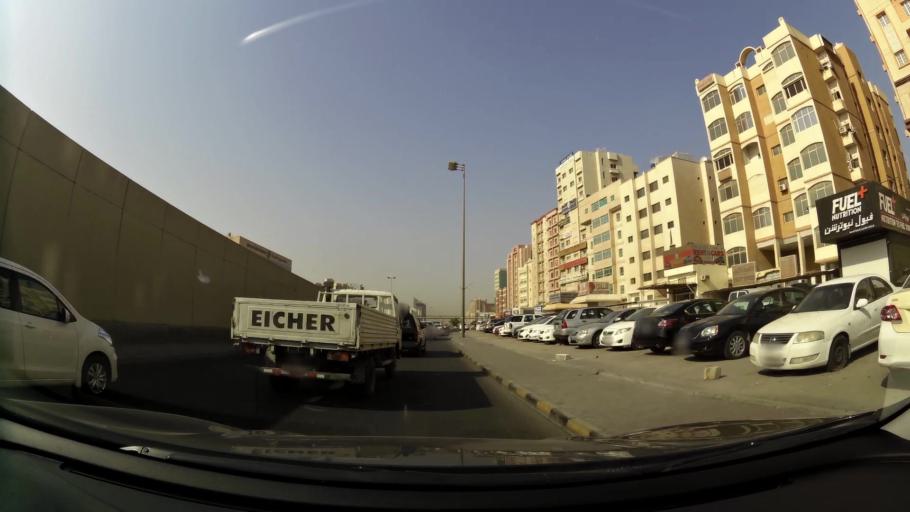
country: KW
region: Muhafazat Hawalli
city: Hawalli
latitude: 29.3280
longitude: 48.0282
